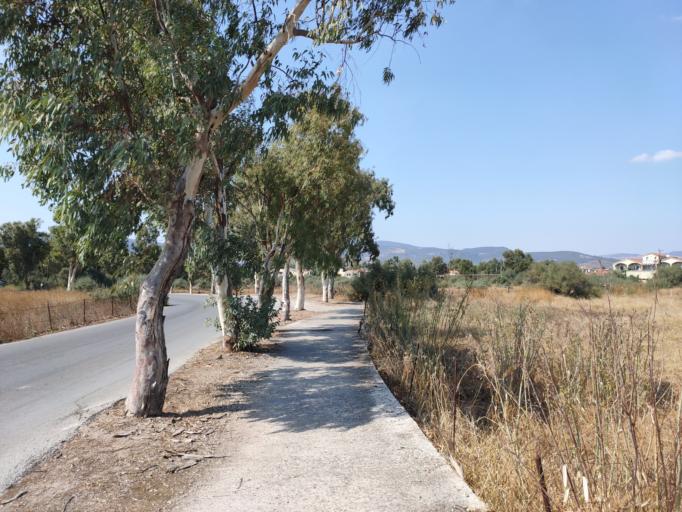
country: GR
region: North Aegean
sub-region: Nomos Lesvou
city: Kalloni
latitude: 39.2088
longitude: 26.2084
